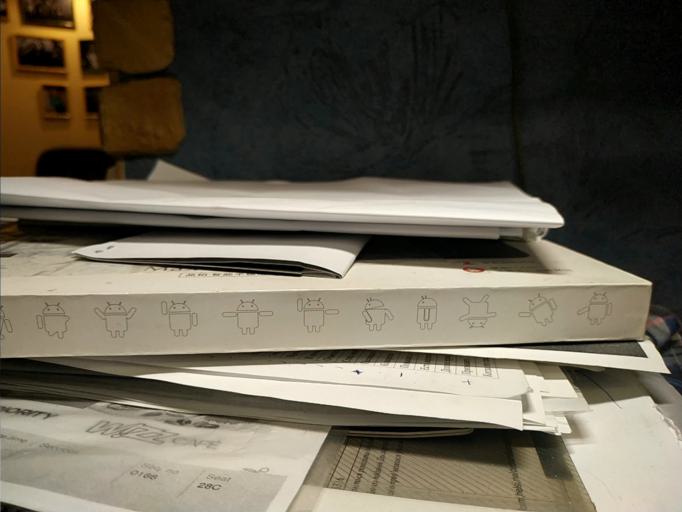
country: RU
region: Tverskaya
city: Zubtsov
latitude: 56.0845
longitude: 34.7776
